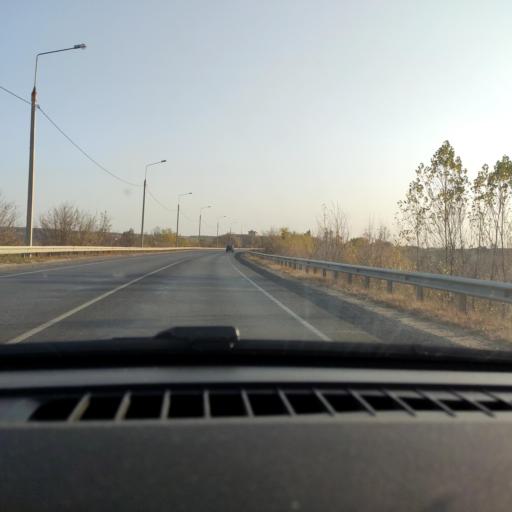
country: RU
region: Voronezj
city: Pridonskoy
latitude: 51.7167
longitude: 39.0742
